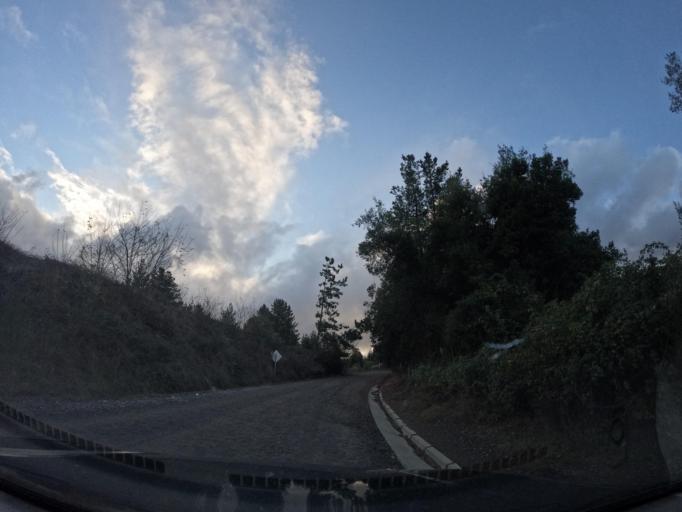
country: CL
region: Biobio
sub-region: Provincia de Concepcion
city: Chiguayante
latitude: -37.0602
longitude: -72.9523
